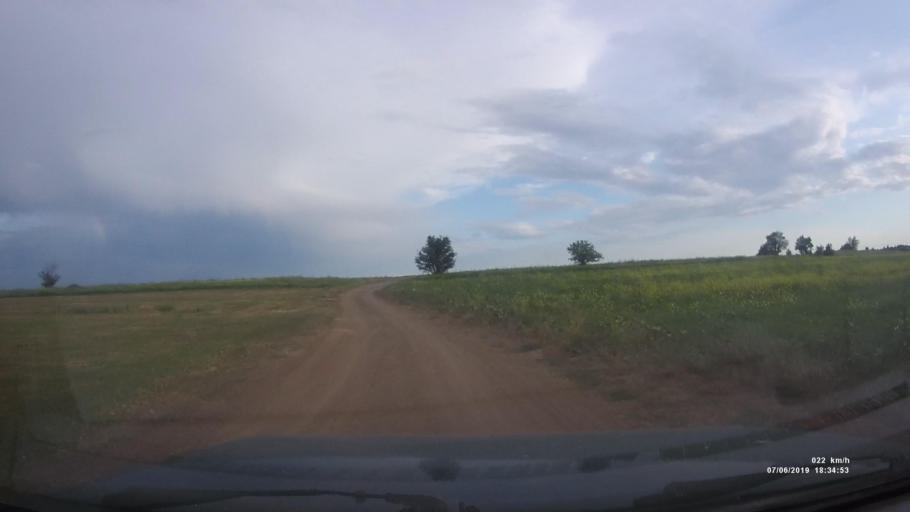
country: RU
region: Rostov
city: Staraya Stanitsa
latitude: 48.2563
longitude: 40.3624
